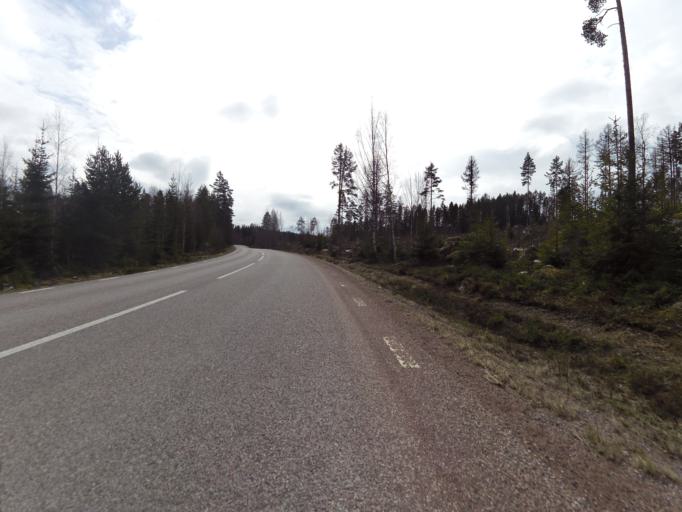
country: SE
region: Dalarna
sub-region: Hedemora Kommun
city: Langshyttan
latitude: 60.5347
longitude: 16.1295
